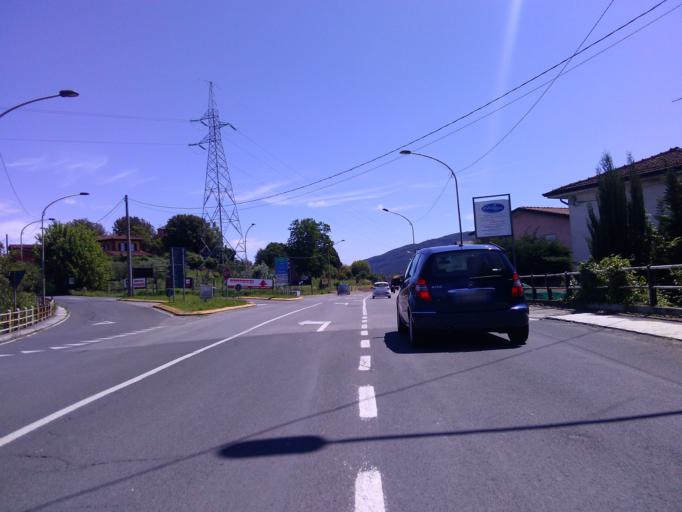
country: IT
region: Liguria
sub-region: Provincia di La Spezia
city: Sarzana
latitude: 44.1215
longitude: 9.9441
